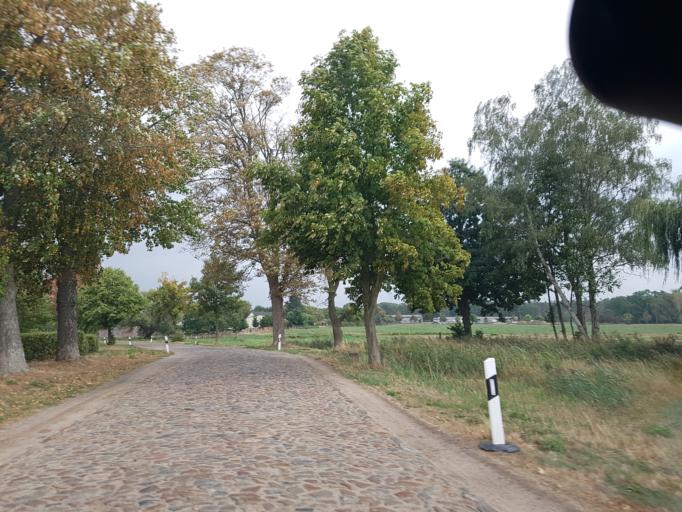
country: DE
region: Saxony-Anhalt
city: Rosslau
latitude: 52.0352
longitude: 12.2812
